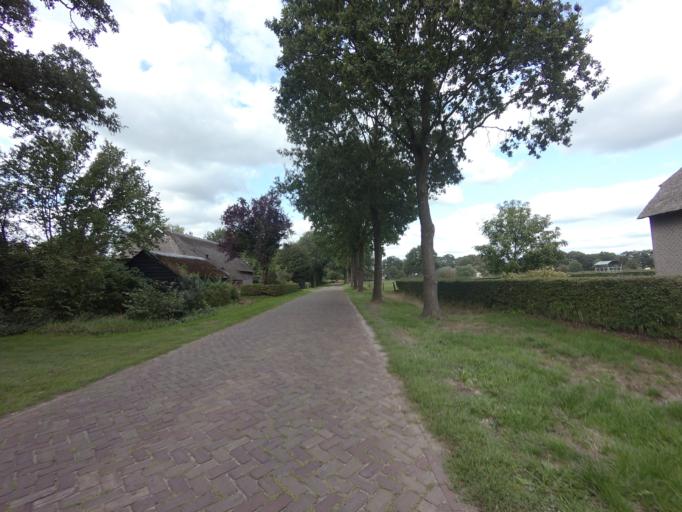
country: NL
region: Drenthe
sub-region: Gemeente De Wolden
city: Ruinen
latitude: 52.7454
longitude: 6.3632
